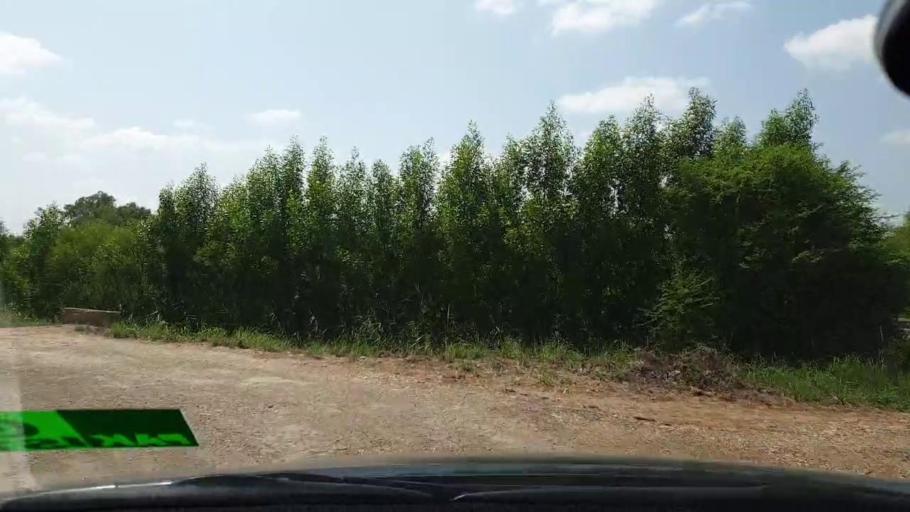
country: PK
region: Sindh
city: Kadhan
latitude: 24.6188
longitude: 69.1843
